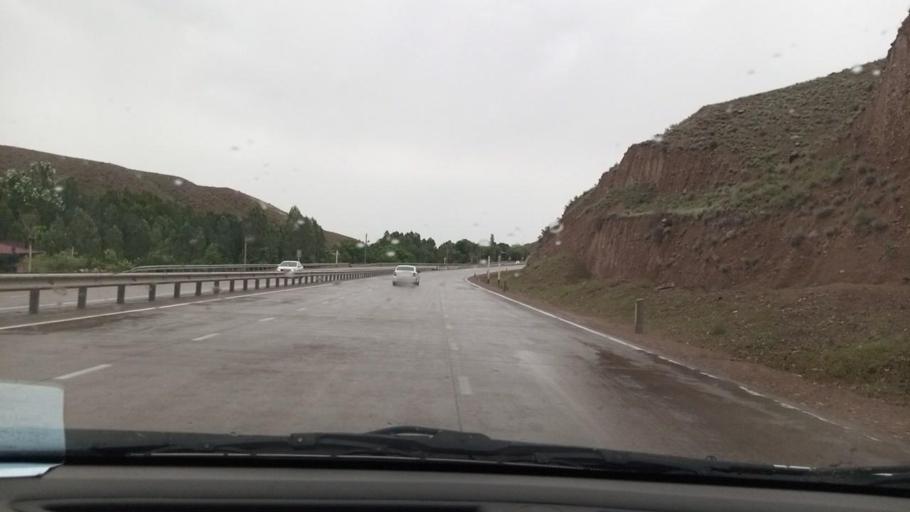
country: UZ
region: Namangan
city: Pop Shahri
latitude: 40.9502
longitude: 70.6785
